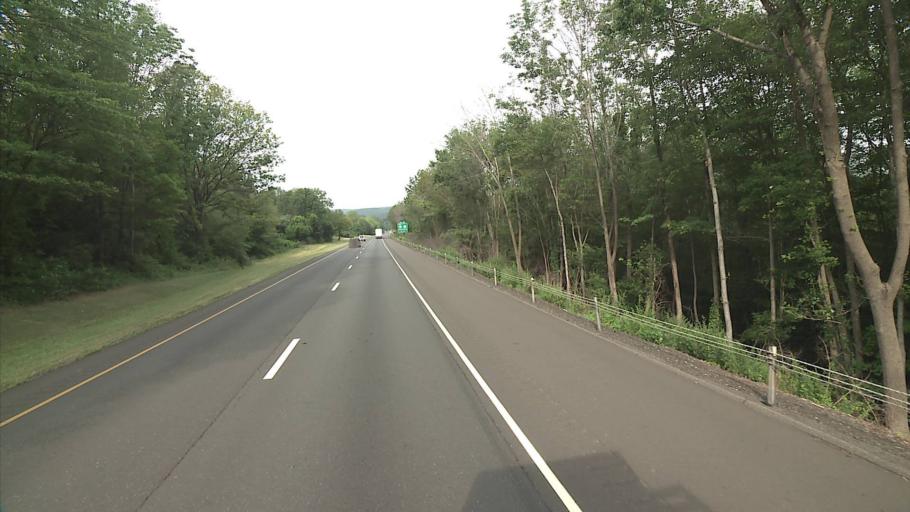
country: US
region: Connecticut
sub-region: New Haven County
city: Southbury
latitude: 41.4815
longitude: -73.1970
